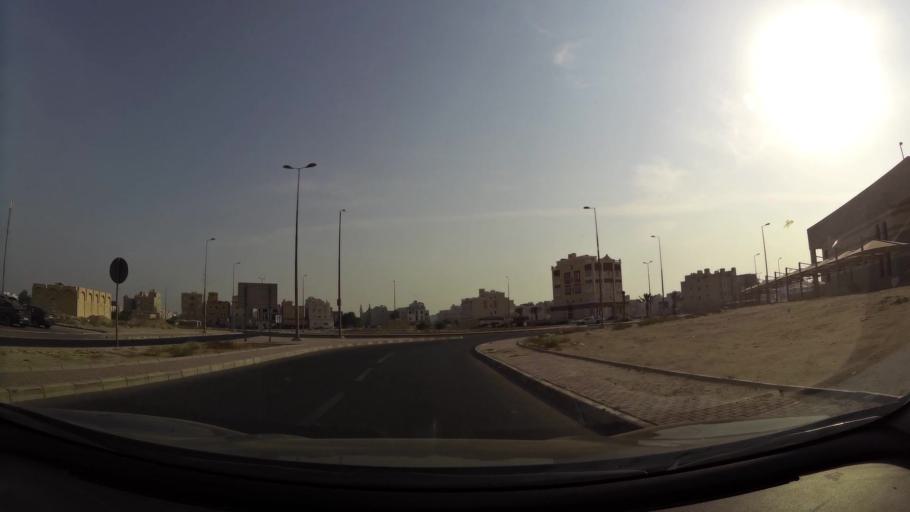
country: KW
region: Mubarak al Kabir
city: Mubarak al Kabir
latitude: 29.1956
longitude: 48.1028
